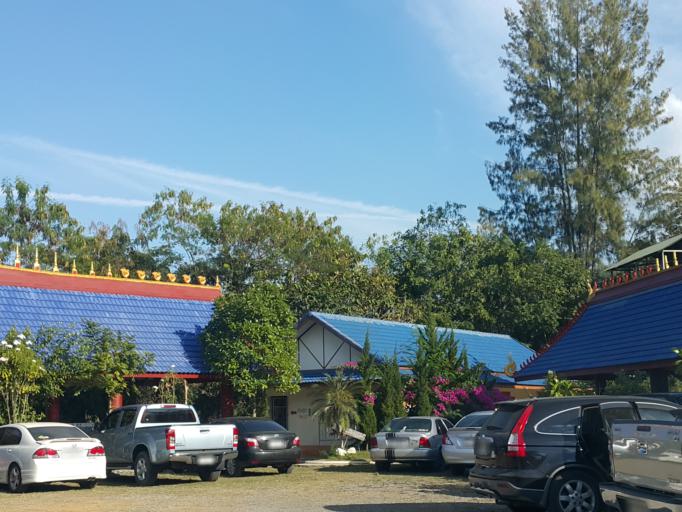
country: TH
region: Sukhothai
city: Thung Saliam
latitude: 17.3233
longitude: 99.5516
